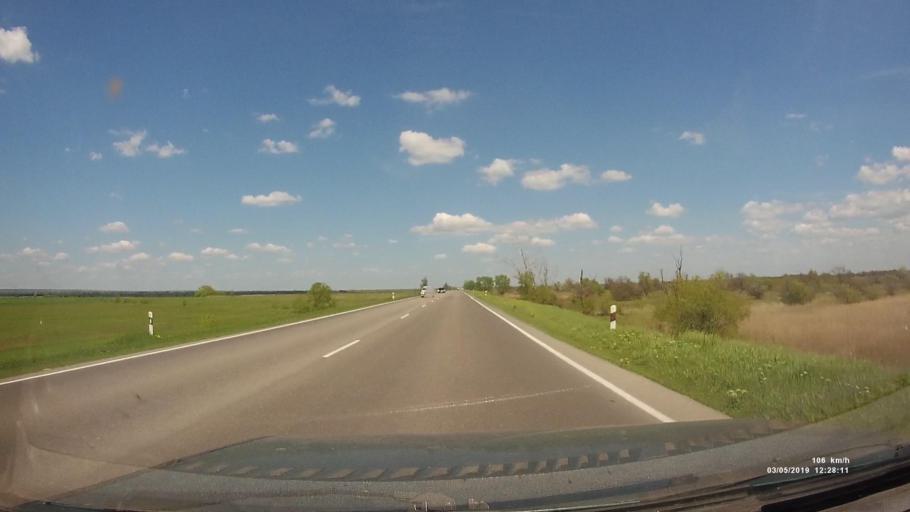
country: RU
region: Rostov
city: Semikarakorsk
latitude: 47.4697
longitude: 40.7263
